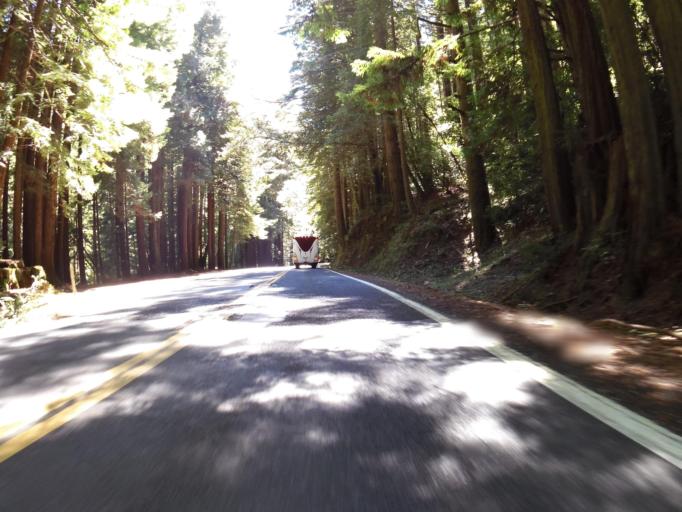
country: US
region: California
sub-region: Humboldt County
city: Redway
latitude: 39.7918
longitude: -123.8174
